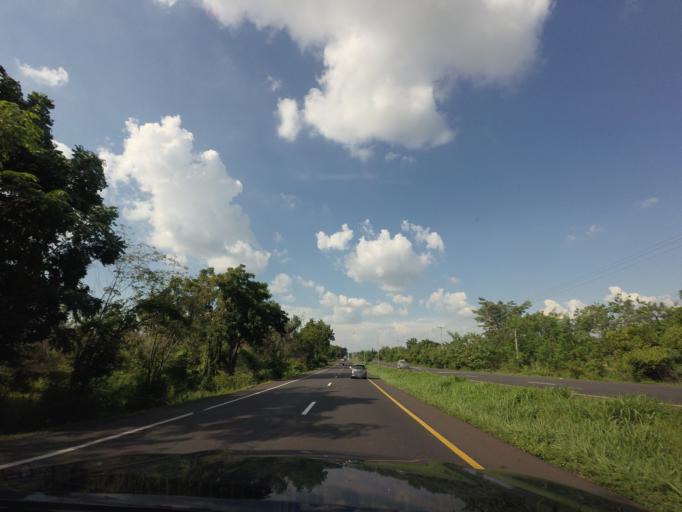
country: TH
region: Nakhon Ratchasima
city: Bua Lai
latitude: 15.6997
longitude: 102.5836
